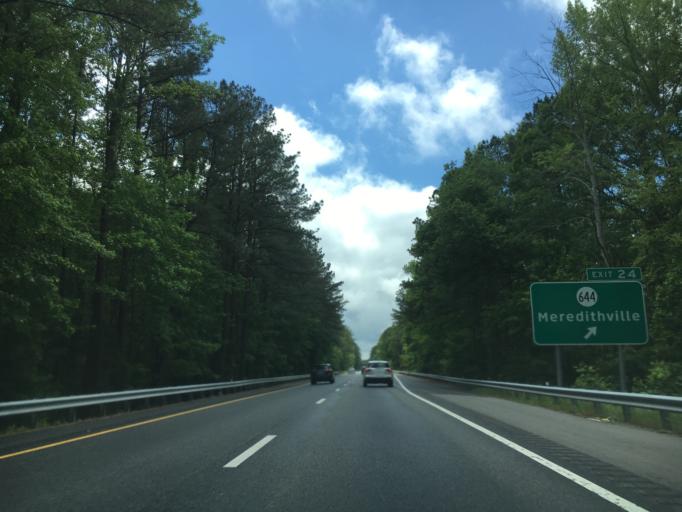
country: US
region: Virginia
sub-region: Brunswick County
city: Lawrenceville
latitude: 36.8255
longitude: -77.9537
